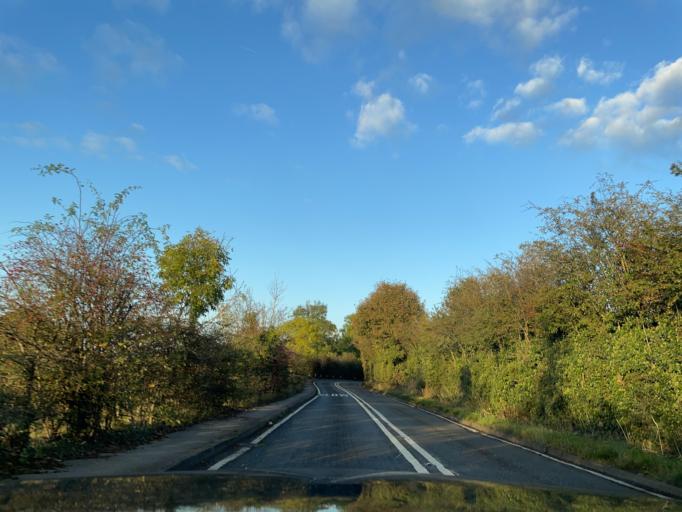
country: GB
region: England
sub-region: Borough of Stockport
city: Marple
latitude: 53.4095
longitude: -2.0400
